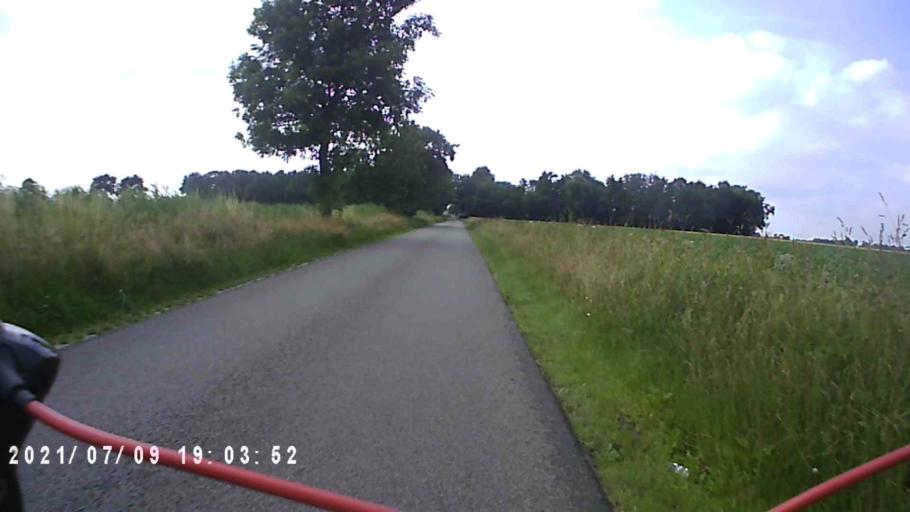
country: NL
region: Groningen
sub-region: Gemeente Veendam
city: Veendam
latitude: 53.0497
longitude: 6.8889
